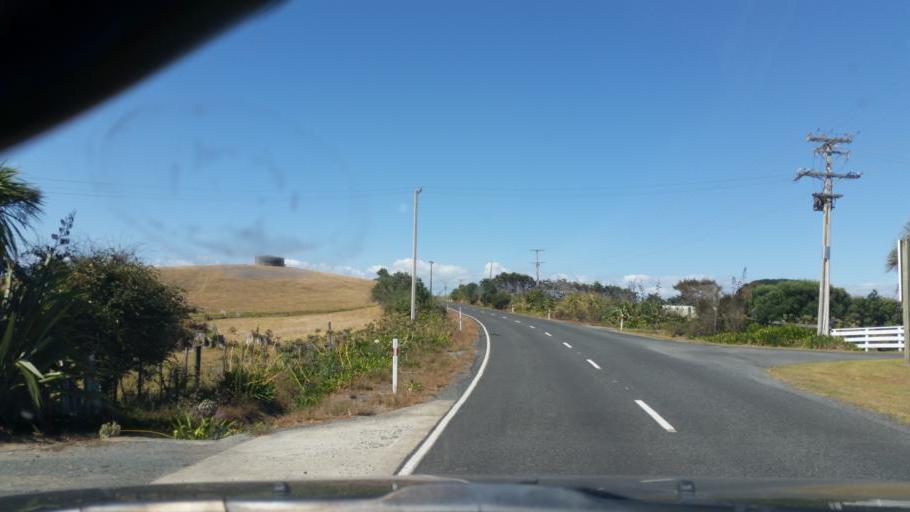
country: NZ
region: Northland
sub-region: Kaipara District
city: Dargaville
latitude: -35.9498
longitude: 173.7571
